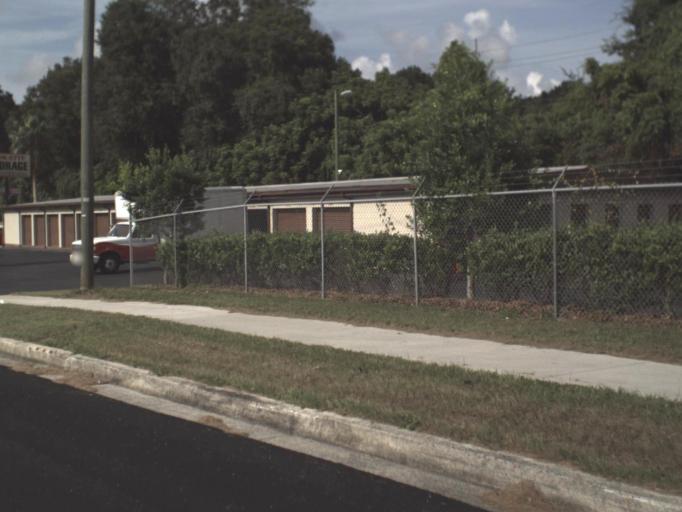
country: US
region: Florida
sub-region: Pasco County
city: Dade City North
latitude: 28.3923
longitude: -82.1951
